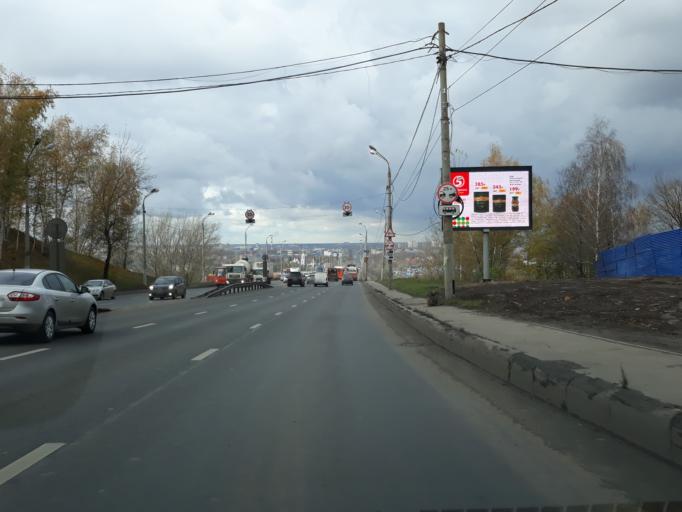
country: RU
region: Nizjnij Novgorod
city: Nizhniy Novgorod
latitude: 56.2465
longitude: 43.9546
